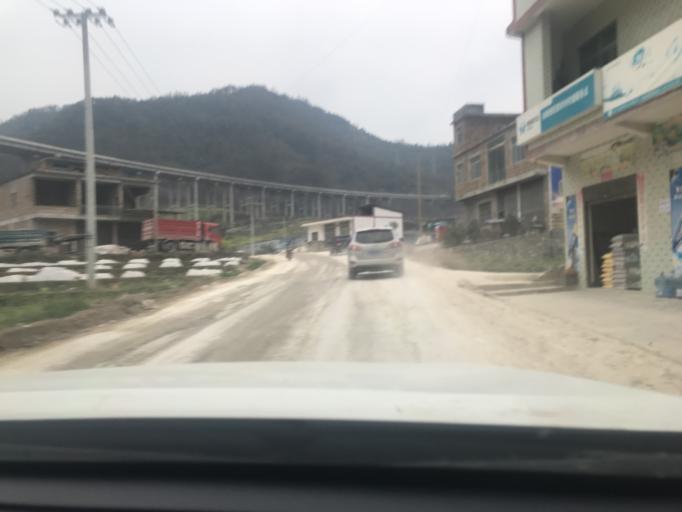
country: CN
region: Guangxi Zhuangzu Zizhiqu
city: Xinzhou
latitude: 25.0086
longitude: 105.8438
